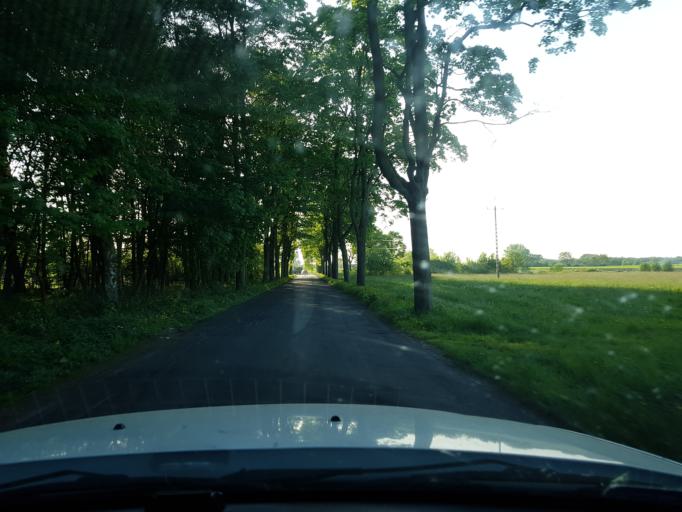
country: PL
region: West Pomeranian Voivodeship
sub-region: Powiat goleniowski
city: Maszewo
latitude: 53.4820
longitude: 14.9911
